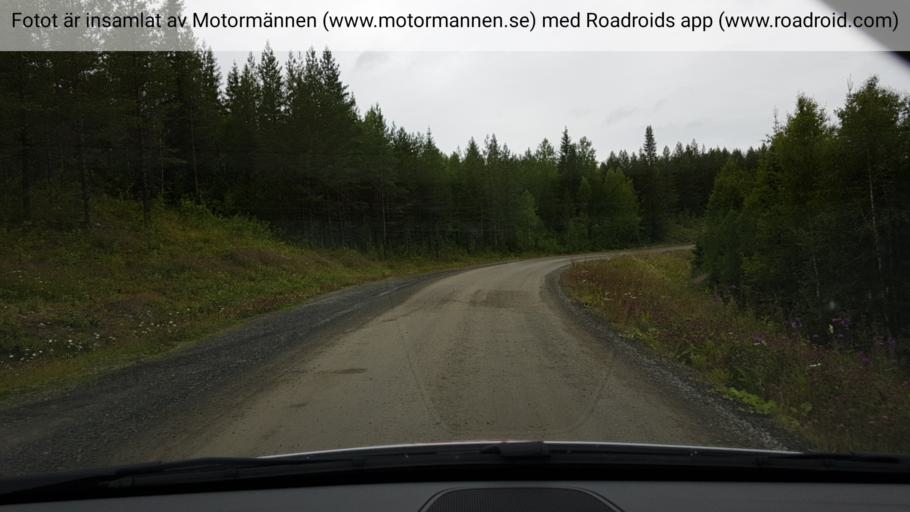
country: SE
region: Jaemtland
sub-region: Krokoms Kommun
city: Krokom
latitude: 63.7292
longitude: 14.5061
